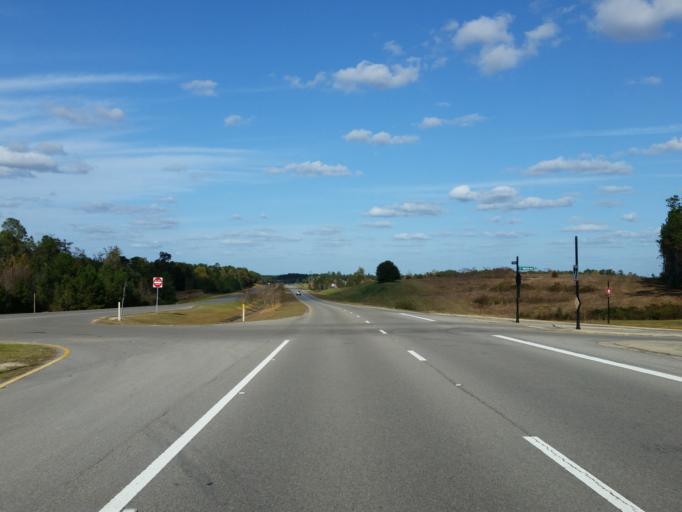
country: US
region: Mississippi
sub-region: Lamar County
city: West Hattiesburg
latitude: 31.2719
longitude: -89.3303
